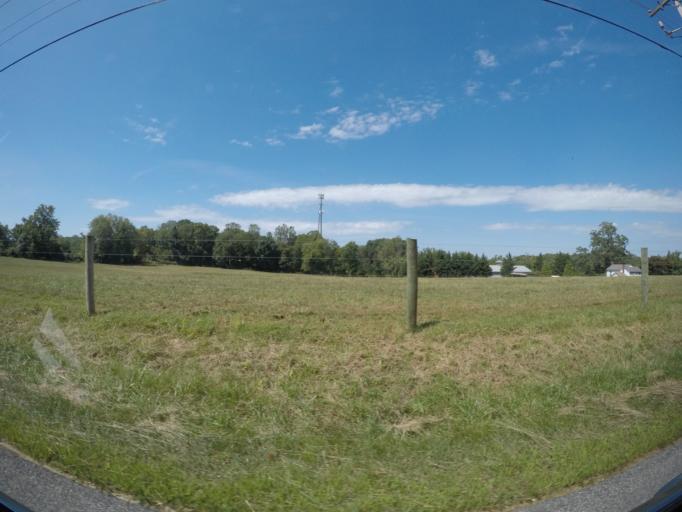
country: US
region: Maryland
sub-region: Harford County
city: South Bel Air
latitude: 39.5694
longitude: -76.3169
